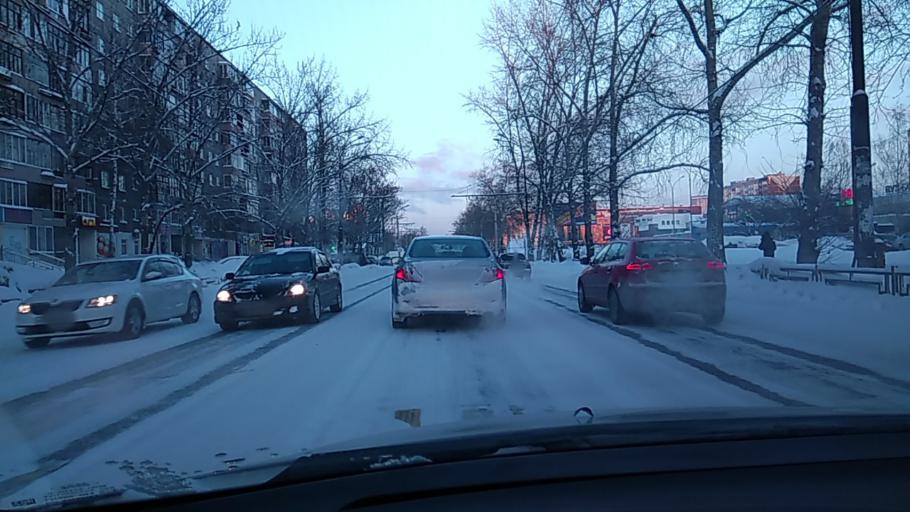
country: RU
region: Sverdlovsk
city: Sovkhoznyy
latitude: 56.7951
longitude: 60.5773
